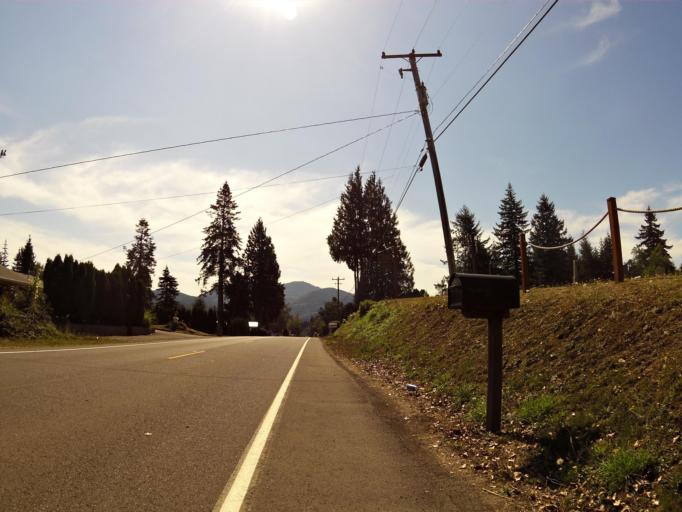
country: US
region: Washington
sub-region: Wahkiakum County
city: Cathlamet
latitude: 46.1741
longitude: -123.5834
